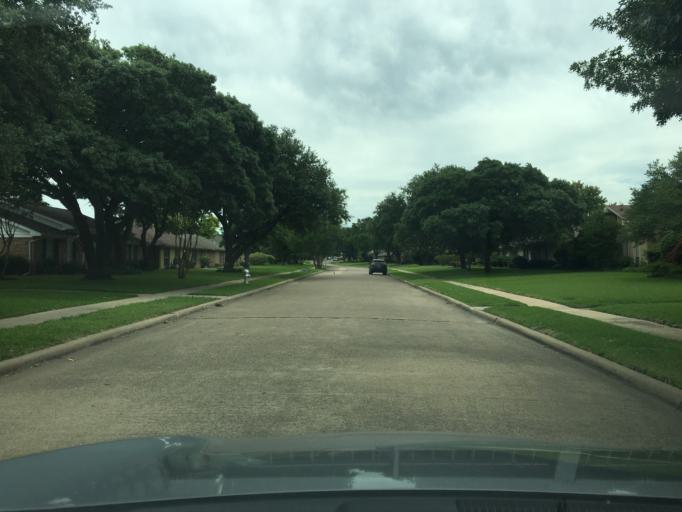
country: US
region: Texas
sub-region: Dallas County
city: Richardson
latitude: 32.9358
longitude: -96.7072
